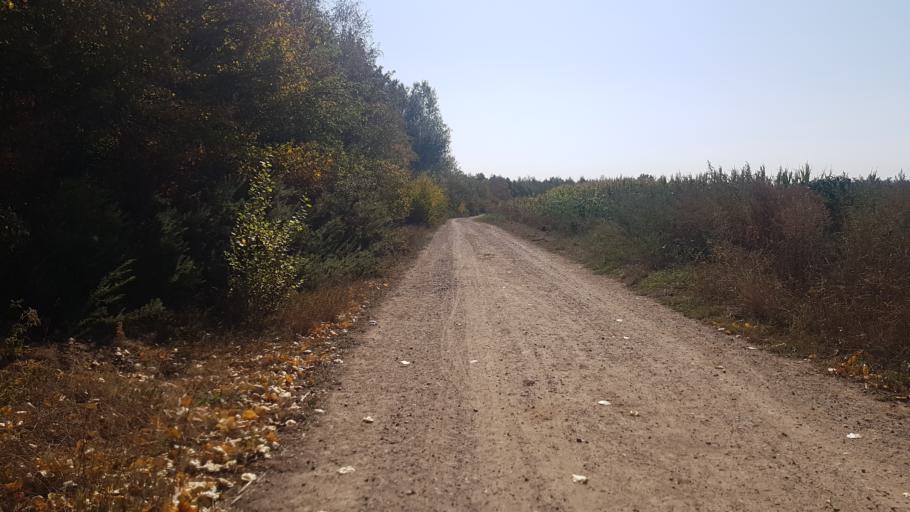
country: DE
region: North Rhine-Westphalia
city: Niedermerz
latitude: 50.8717
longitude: 6.2581
